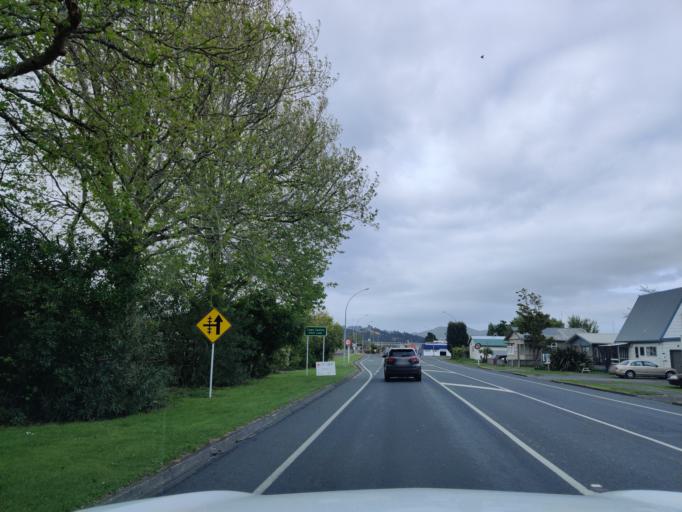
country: NZ
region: Waikato
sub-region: Waikato District
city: Ngaruawahia
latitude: -37.5522
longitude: 175.1588
